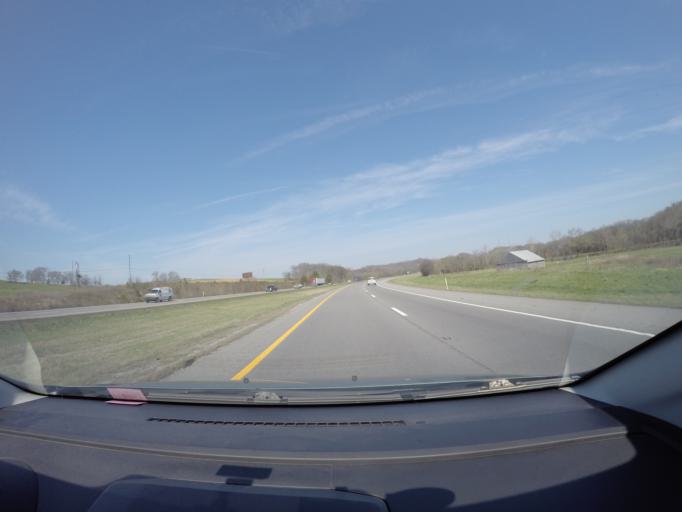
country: US
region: Tennessee
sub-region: Coffee County
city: New Union
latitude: 35.5698
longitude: -86.2285
